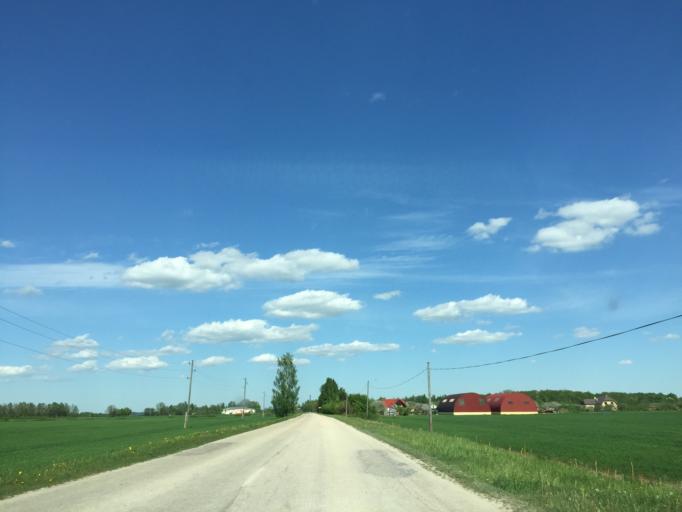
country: LV
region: Bauskas Rajons
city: Bauska
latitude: 56.3934
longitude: 24.1104
